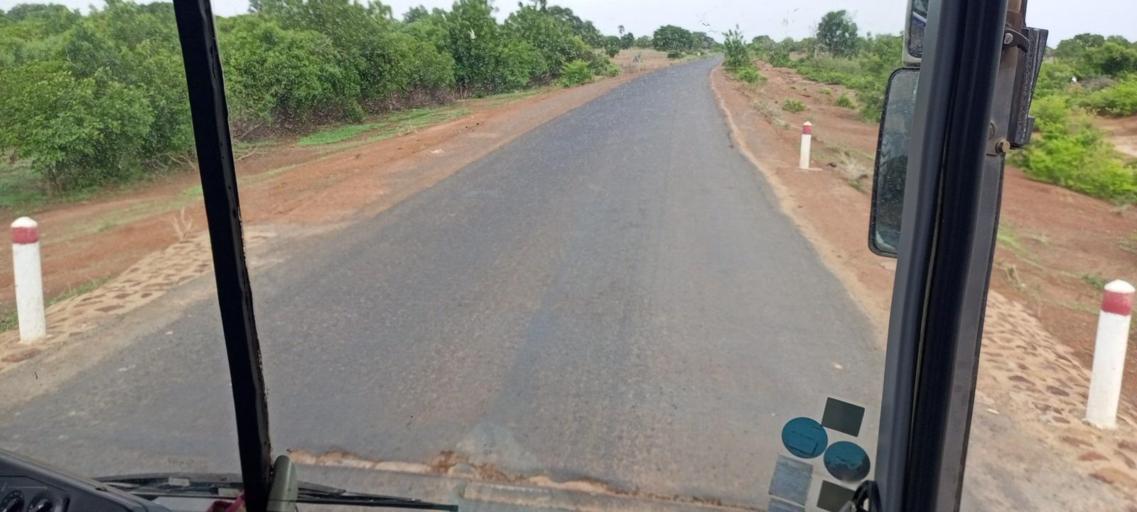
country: ML
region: Segou
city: Bla
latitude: 12.7324
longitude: -5.7256
